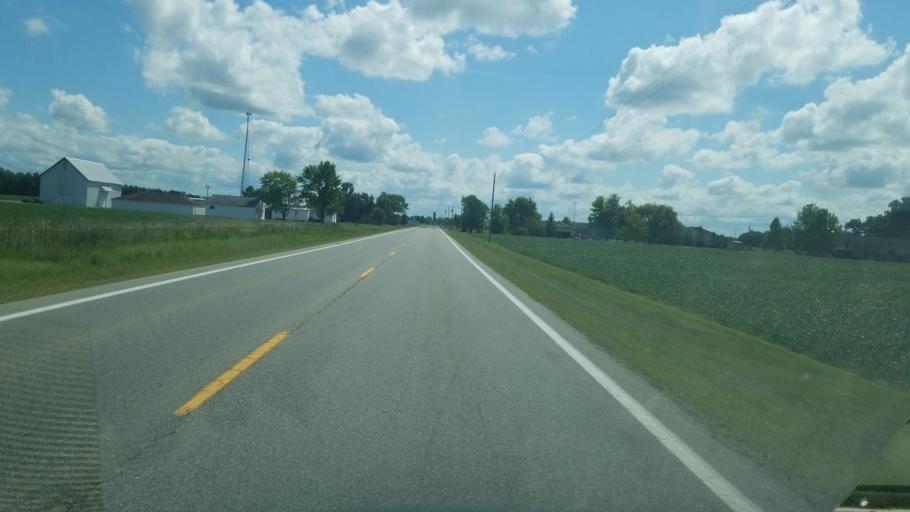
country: US
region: Ohio
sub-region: Putnam County
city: Kalida
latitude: 41.0059
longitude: -84.1979
